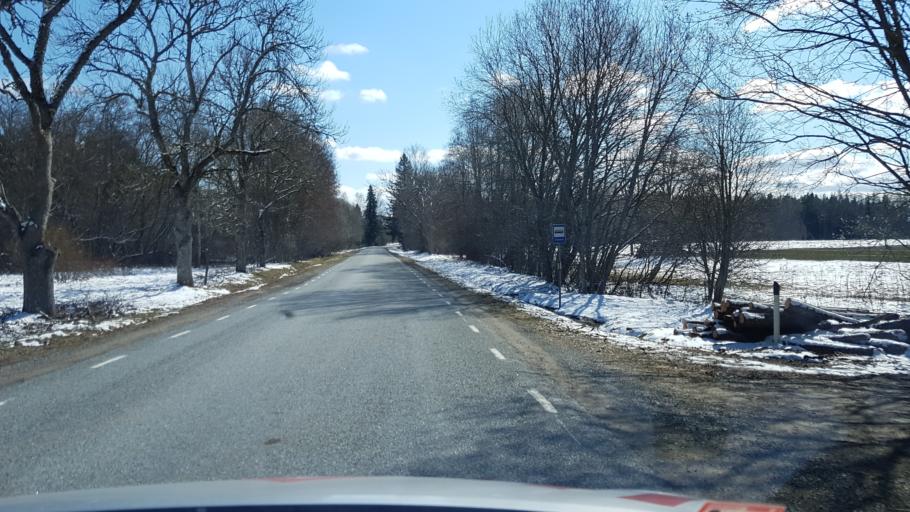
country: EE
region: Laeaene-Virumaa
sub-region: Kadrina vald
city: Kadrina
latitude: 59.4960
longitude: 25.9743
